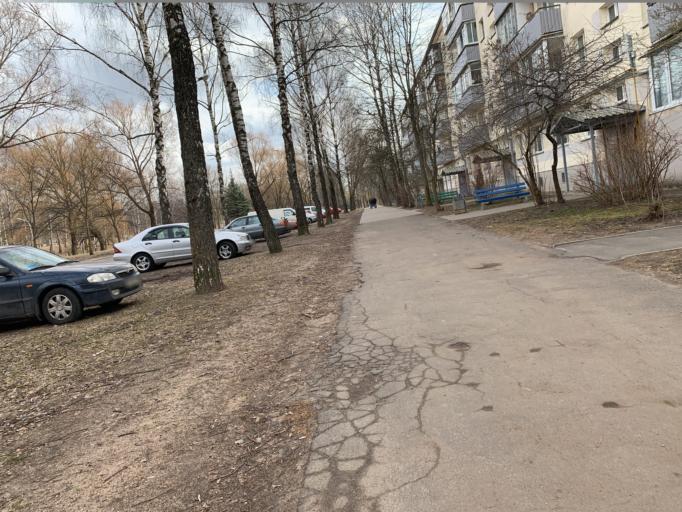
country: BY
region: Minsk
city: Borovlyany
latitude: 53.9521
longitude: 27.6266
